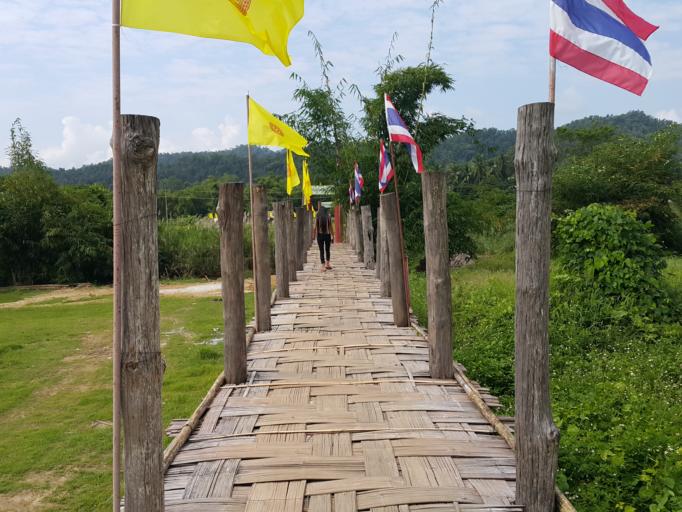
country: TH
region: Mae Hong Son
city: Mae Hong Son
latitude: 19.3893
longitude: 97.9547
